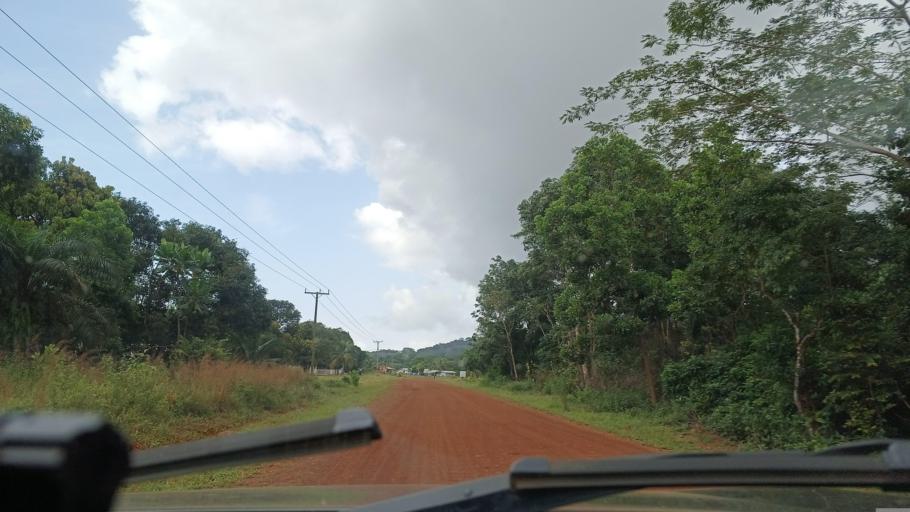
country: LR
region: Grand Cape Mount
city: Robertsport
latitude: 6.7053
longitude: -11.3305
